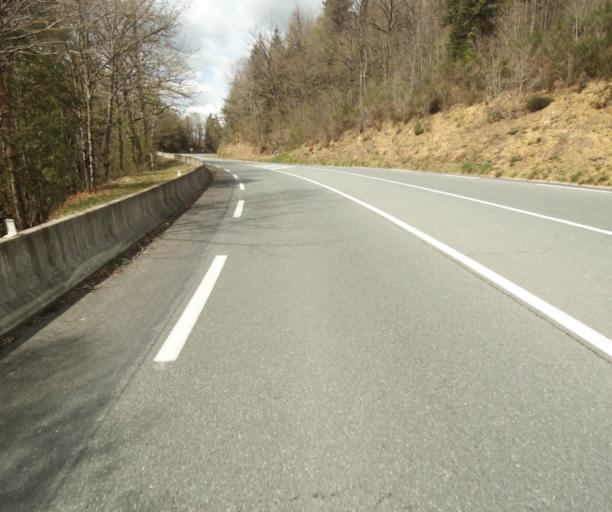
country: FR
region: Limousin
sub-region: Departement de la Correze
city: Sainte-Fortunade
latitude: 45.1944
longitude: 1.8391
